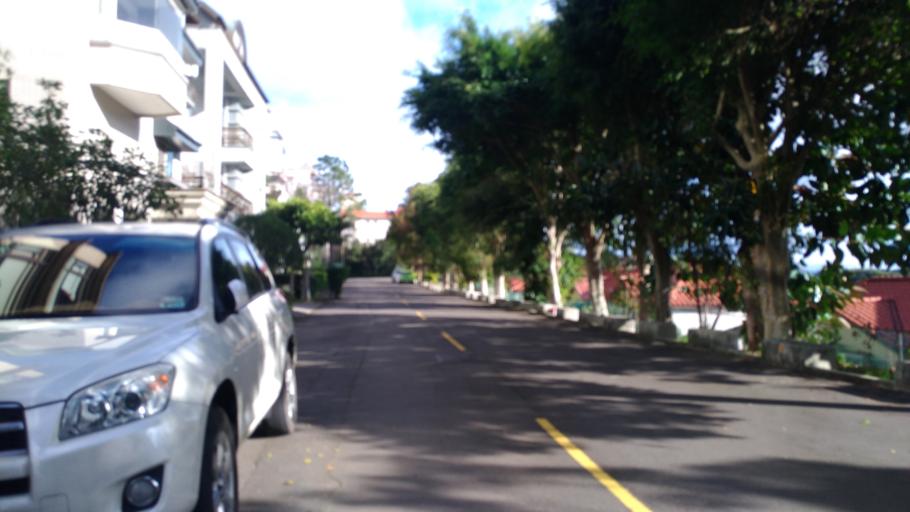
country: TW
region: Taiwan
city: Daxi
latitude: 24.8848
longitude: 121.1693
